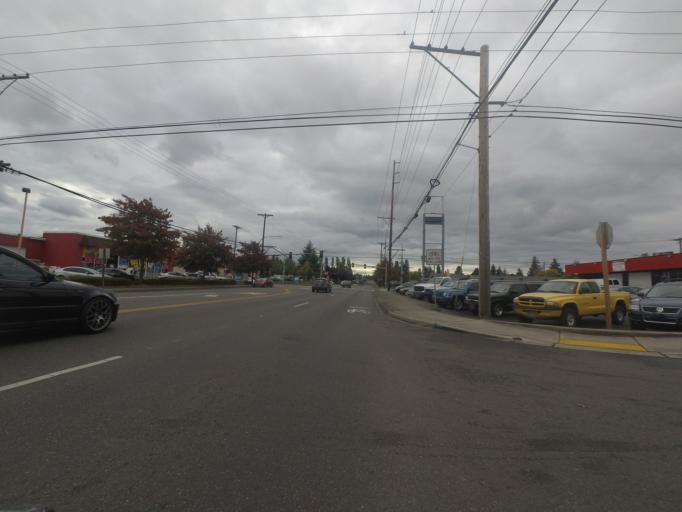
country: US
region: Washington
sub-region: Pierce County
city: Lakewood
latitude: 47.1565
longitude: -122.5046
